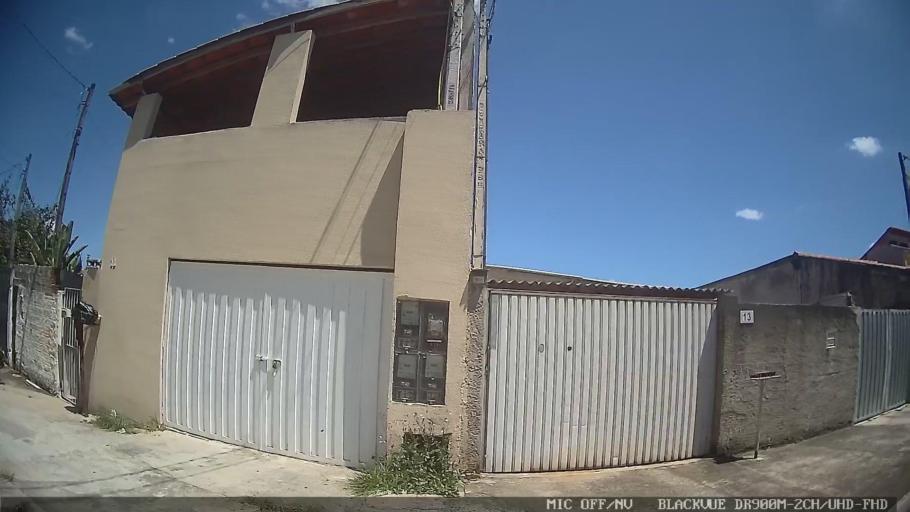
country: BR
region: Sao Paulo
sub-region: Atibaia
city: Atibaia
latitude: -23.1017
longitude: -46.5641
